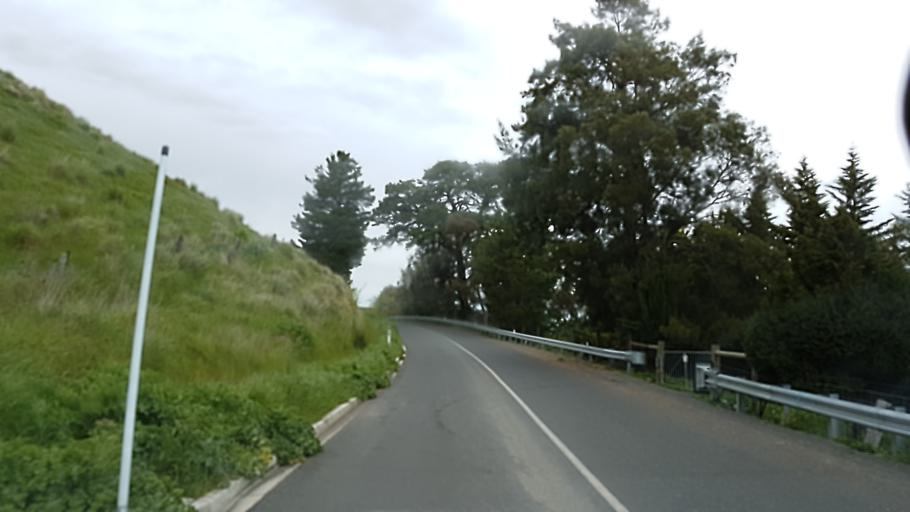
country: AU
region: Victoria
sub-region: Ballarat North
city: Mount Clear
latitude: -37.7825
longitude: 144.1009
